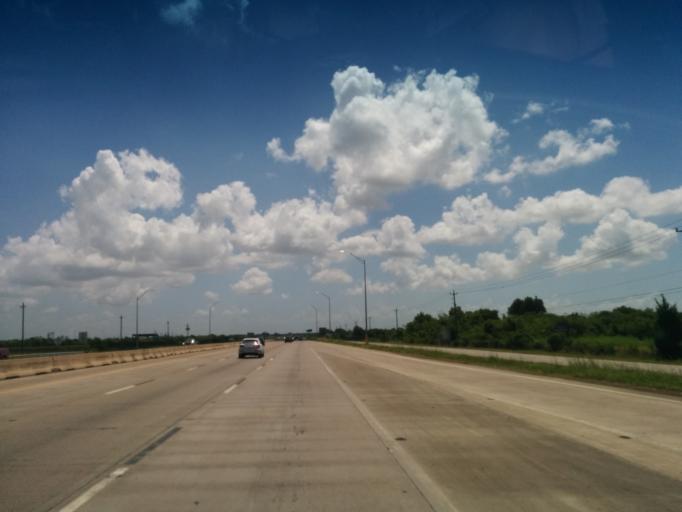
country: US
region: Texas
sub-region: Harris County
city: Baytown
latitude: 29.8086
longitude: -94.9599
